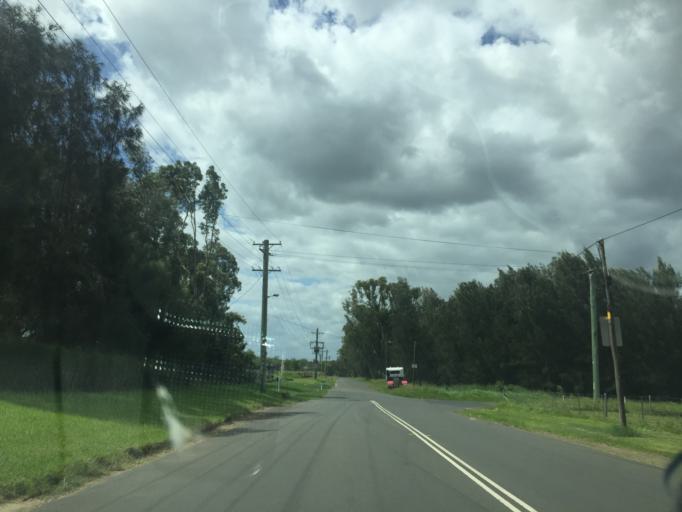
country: AU
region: New South Wales
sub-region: Penrith Municipality
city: Kingswood Park
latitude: -33.7890
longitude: 150.7383
